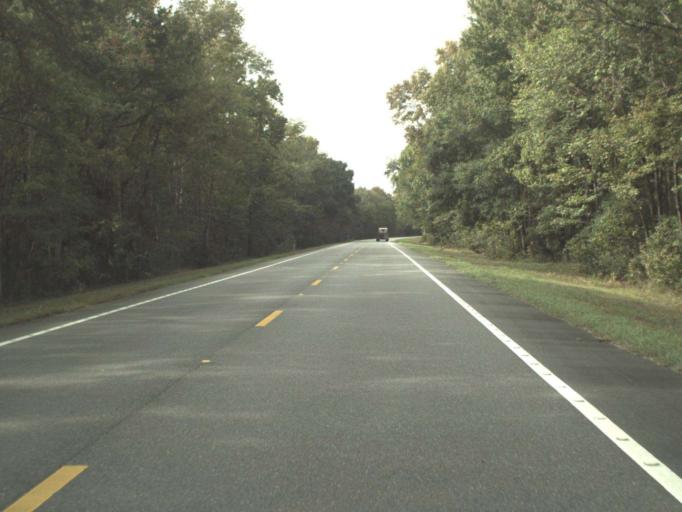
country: US
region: Florida
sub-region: Leon County
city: Woodville
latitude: 30.1563
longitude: -83.9949
